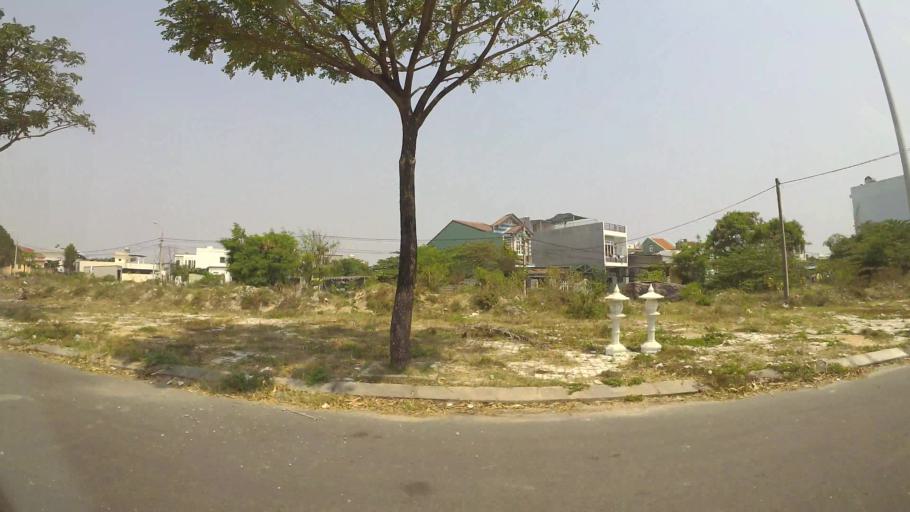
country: VN
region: Da Nang
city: Ngu Hanh Son
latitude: 16.0058
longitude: 108.2574
